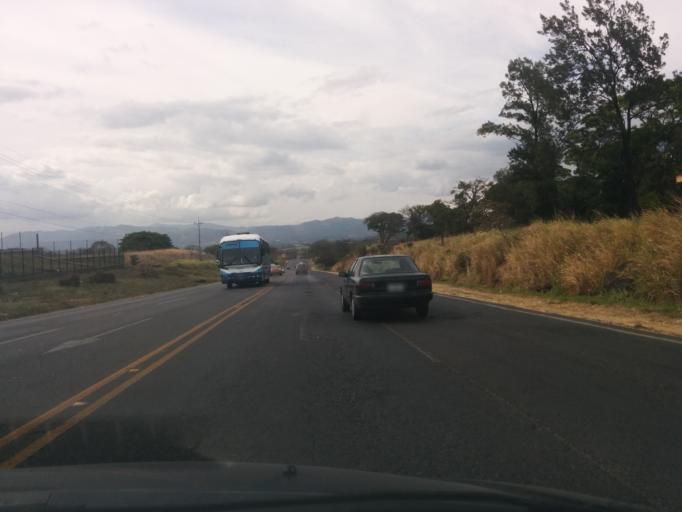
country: CR
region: Alajuela
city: Carrillos
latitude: 9.9989
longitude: -84.2775
